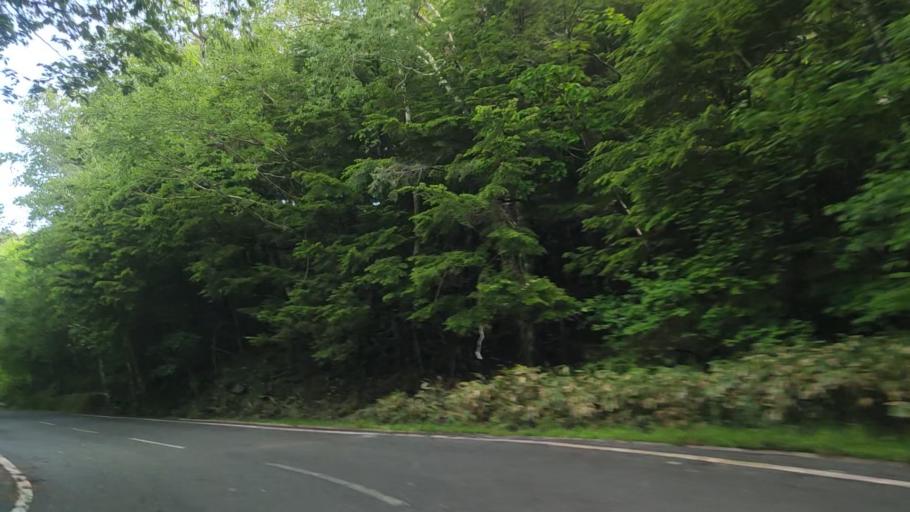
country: JP
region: Nagano
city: Chino
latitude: 36.1143
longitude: 138.2748
